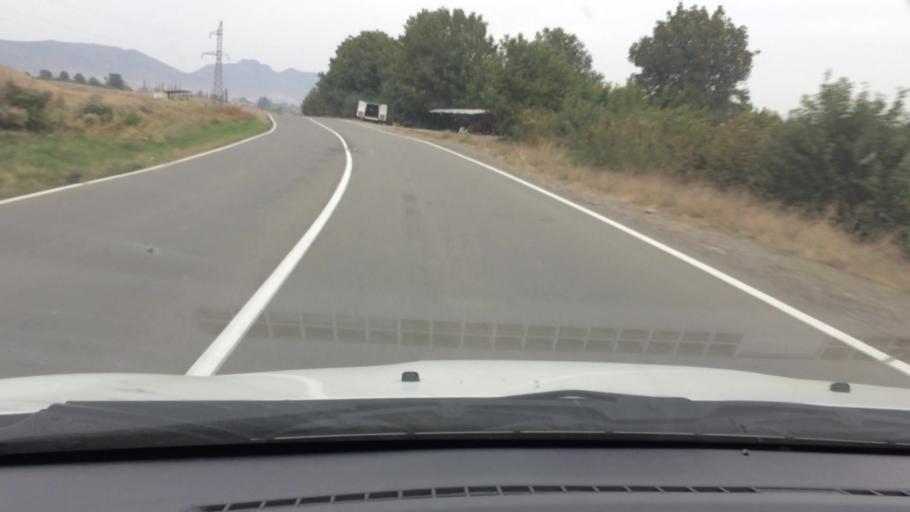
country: AM
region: Tavush
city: Bagratashen
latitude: 41.2849
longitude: 44.7904
